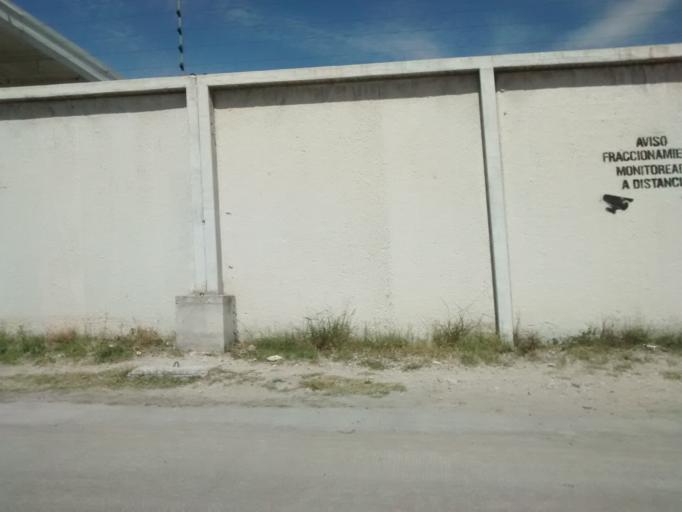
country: MX
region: Puebla
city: Tehuacan
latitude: 18.4709
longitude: -97.4146
